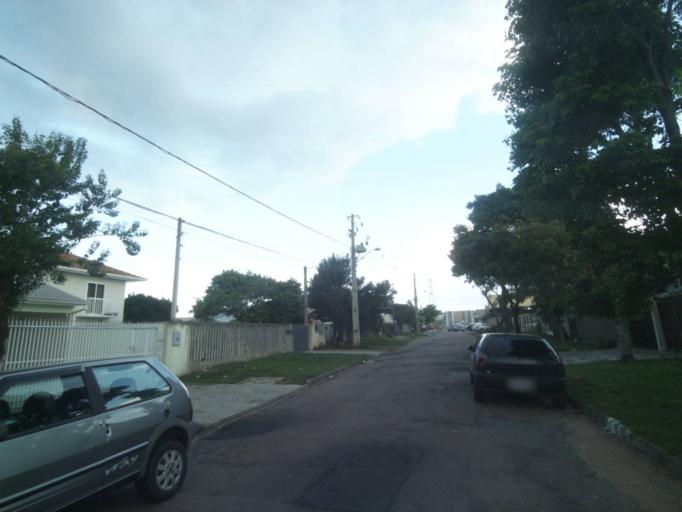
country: BR
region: Parana
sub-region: Sao Jose Dos Pinhais
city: Sao Jose dos Pinhais
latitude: -25.5337
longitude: -49.2729
